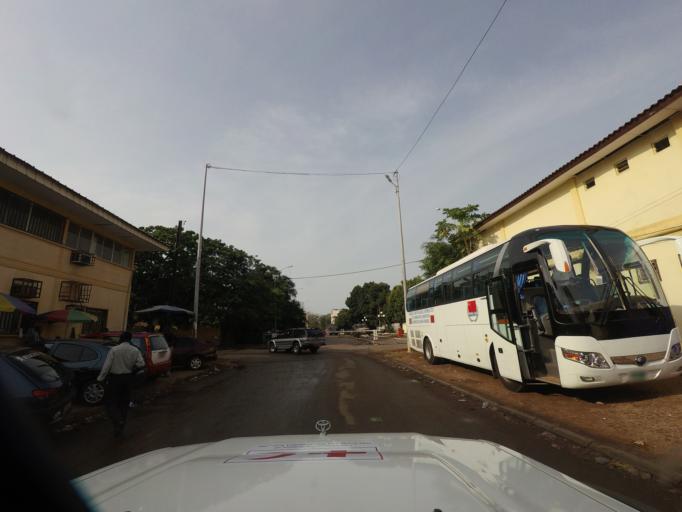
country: GN
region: Conakry
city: Camayenne
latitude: 9.5108
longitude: -13.7161
